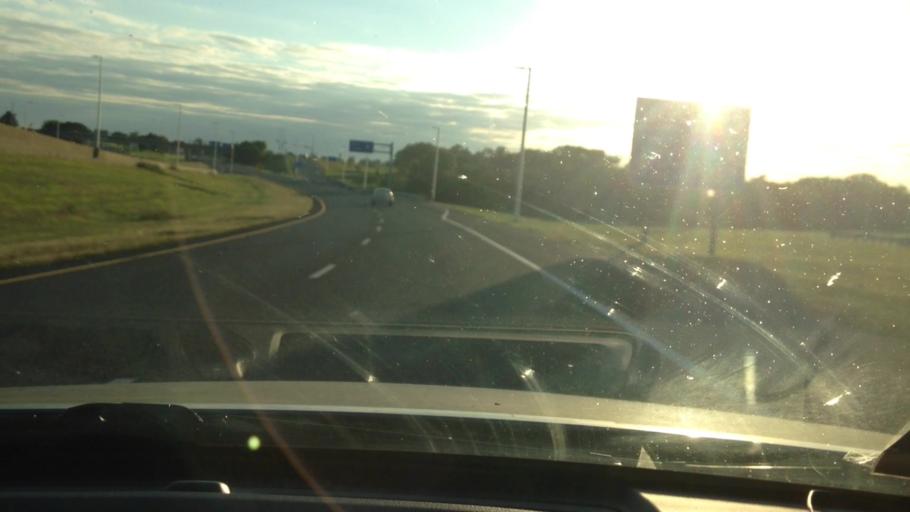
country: US
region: Missouri
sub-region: Platte County
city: Weatherby Lake
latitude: 39.3111
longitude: -94.7027
